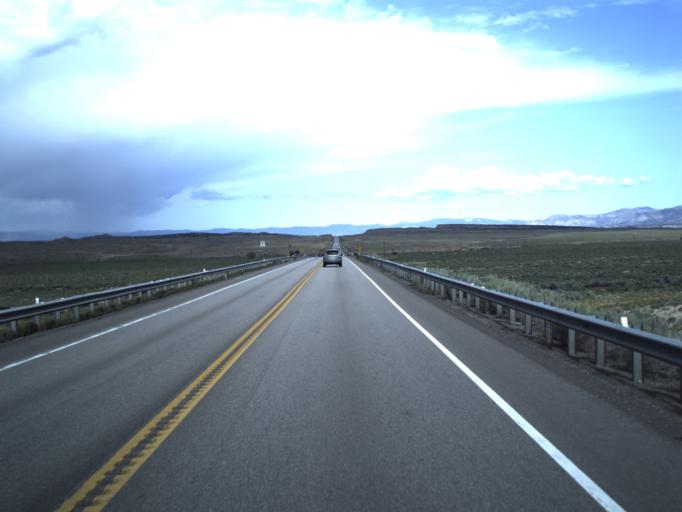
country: US
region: Utah
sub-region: Carbon County
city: East Carbon City
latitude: 39.5210
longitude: -110.5624
